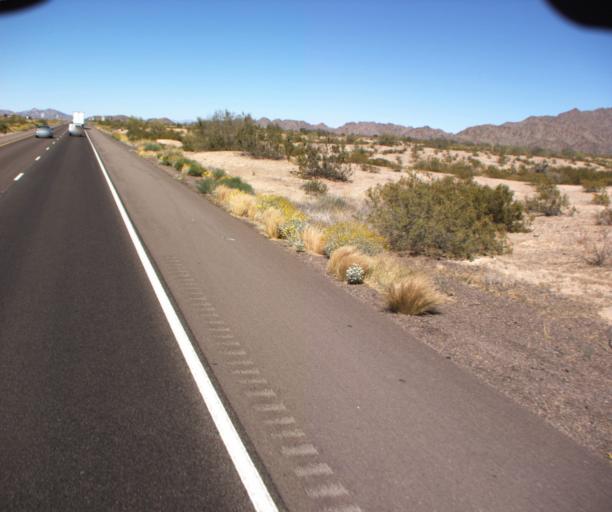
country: US
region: Arizona
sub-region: Maricopa County
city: Gila Bend
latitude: 33.1265
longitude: -112.6501
